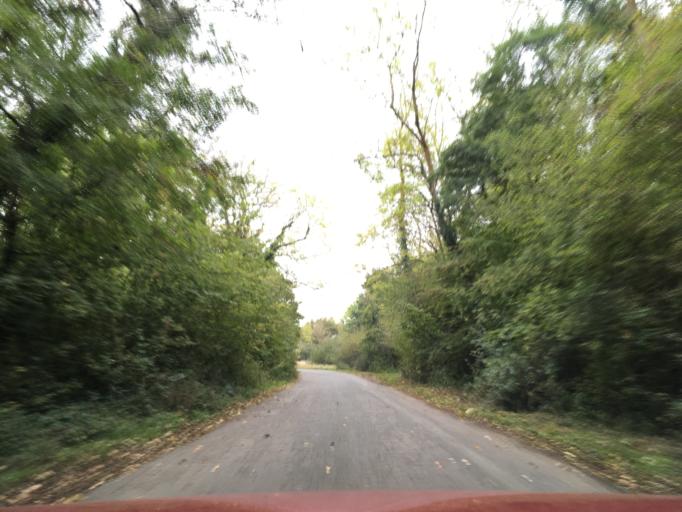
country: GB
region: England
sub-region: South Gloucestershire
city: Horton
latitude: 51.5925
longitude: -2.3583
